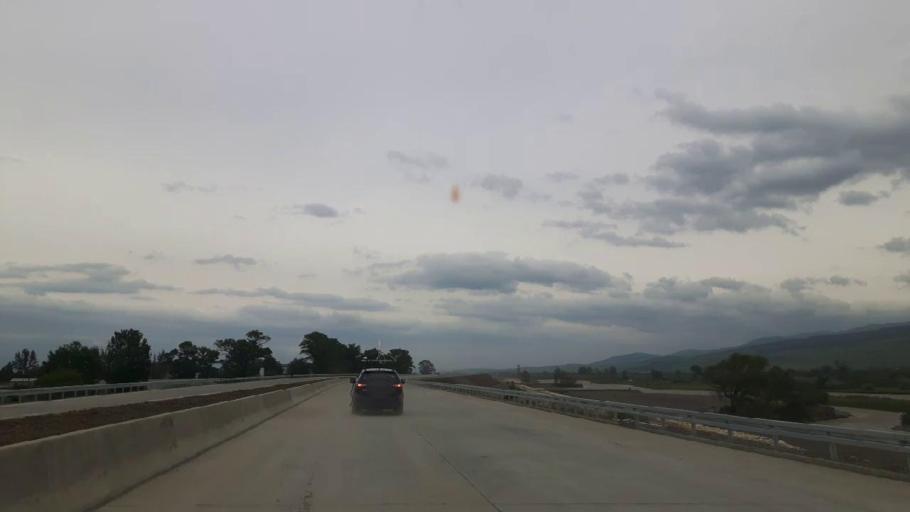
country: GE
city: Agara
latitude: 42.0163
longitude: 43.7332
